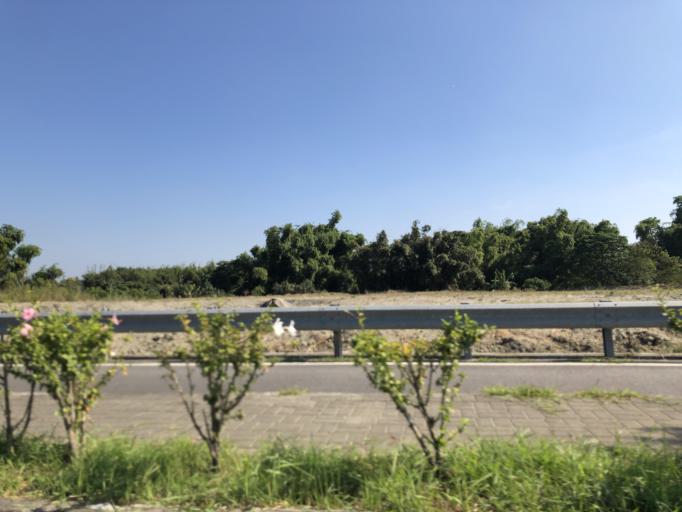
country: TW
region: Taiwan
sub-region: Tainan
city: Tainan
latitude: 23.0309
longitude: 120.3224
